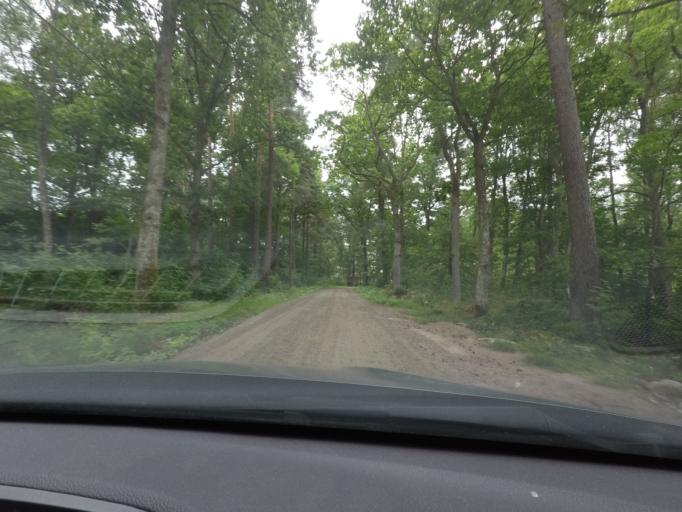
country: SE
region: Skane
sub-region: Osby Kommun
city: Osby
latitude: 56.3553
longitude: 13.9942
